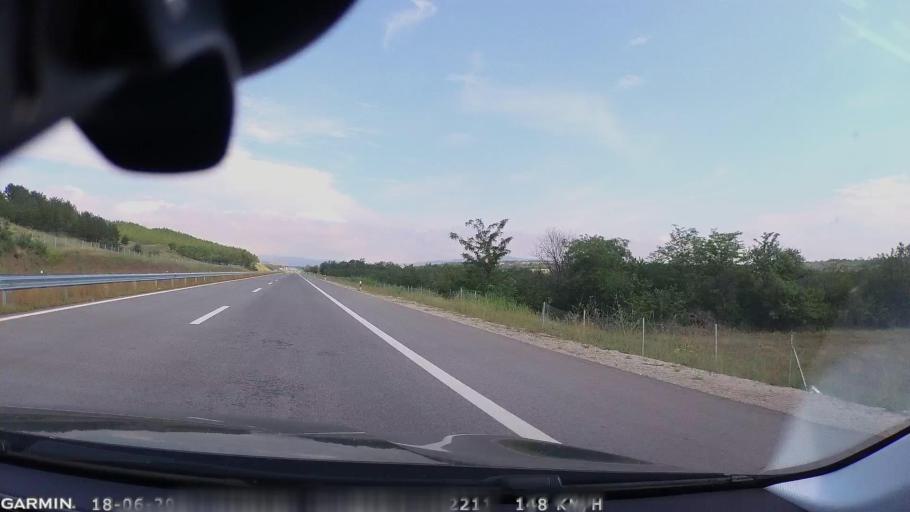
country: MK
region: Sveti Nikole
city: Sveti Nikole
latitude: 41.8972
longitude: 21.9204
